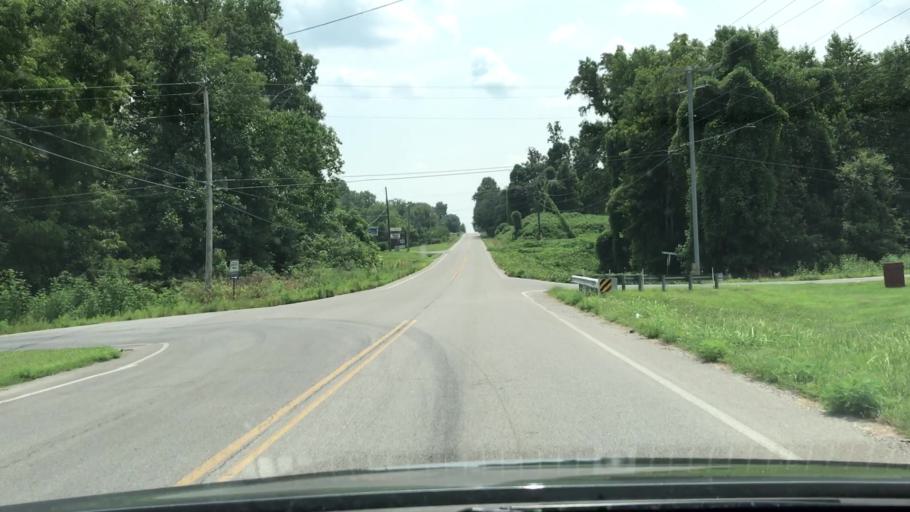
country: US
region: Tennessee
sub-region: Sumner County
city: Portland
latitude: 36.5230
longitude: -86.5018
